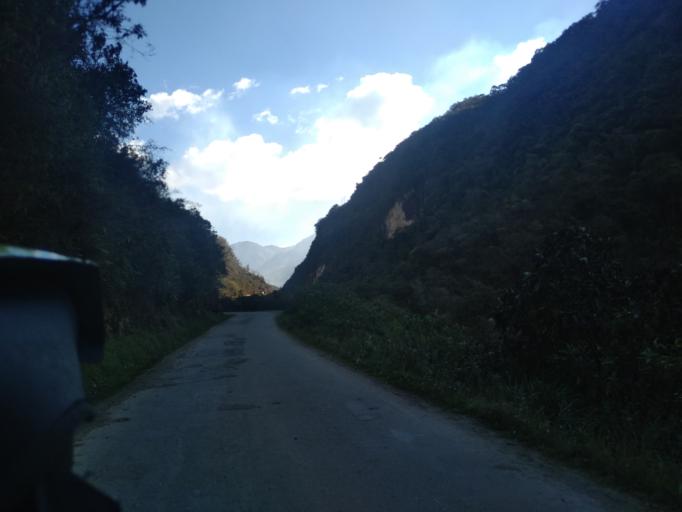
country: PE
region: Amazonas
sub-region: Provincia de Chachapoyas
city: Montevideo
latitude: -6.7225
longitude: -77.8244
